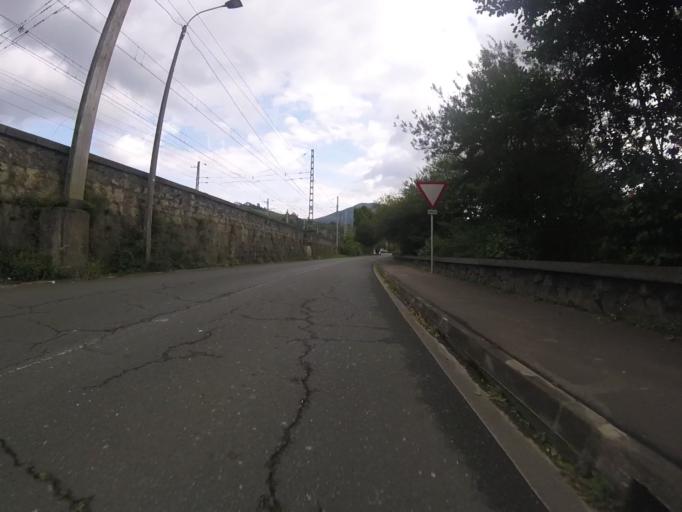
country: ES
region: Basque Country
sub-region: Provincia de Guipuzcoa
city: Tolosa
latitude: 43.1325
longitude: -2.0845
